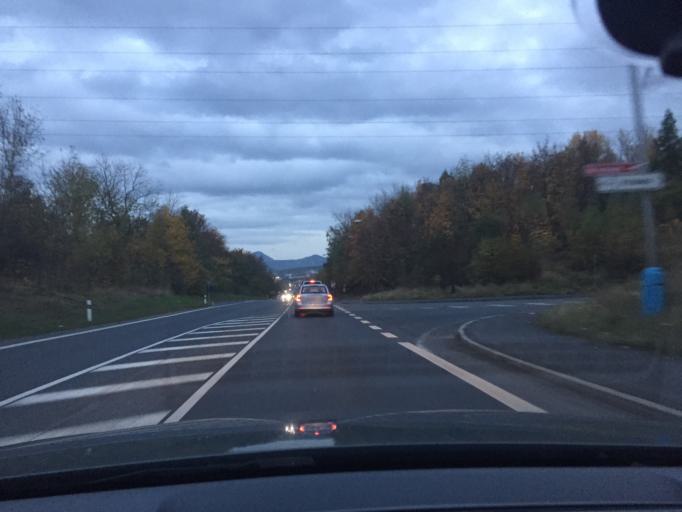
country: CZ
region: Ustecky
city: Novosedlice
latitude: 50.6516
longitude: 13.8107
